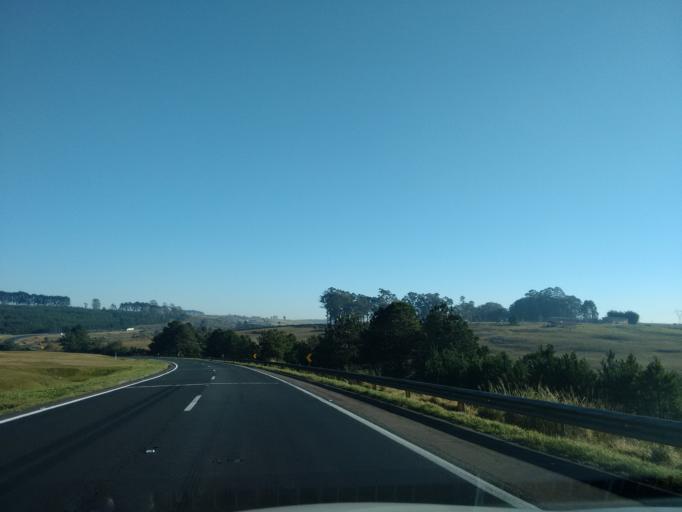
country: BR
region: Parana
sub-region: Campo Largo
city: Campo Largo
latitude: -25.4439
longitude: -49.7437
